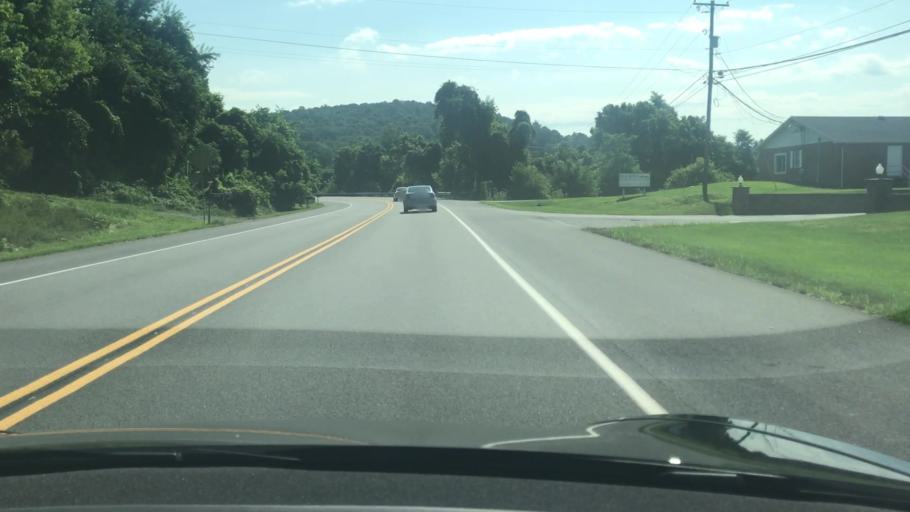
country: US
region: Pennsylvania
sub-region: York County
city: Valley Green
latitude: 40.1309
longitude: -76.8196
